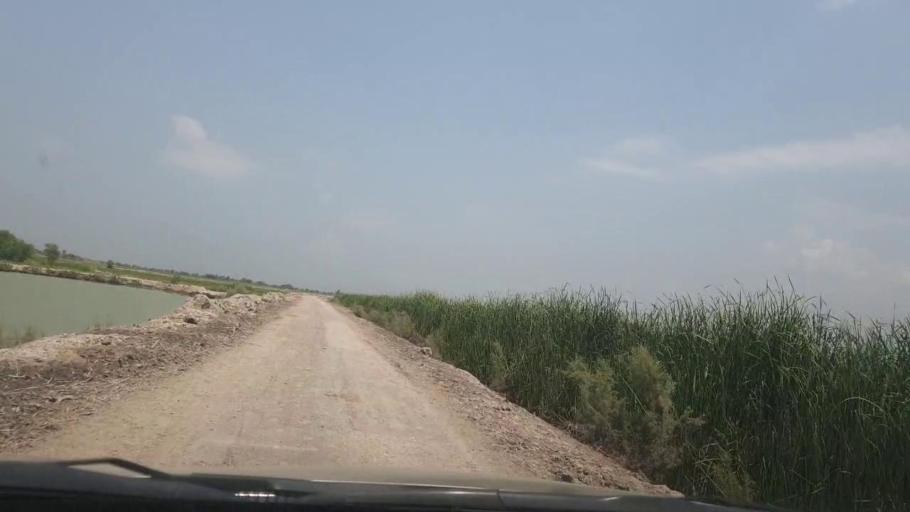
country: PK
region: Sindh
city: Ratodero
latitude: 27.7167
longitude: 68.2901
